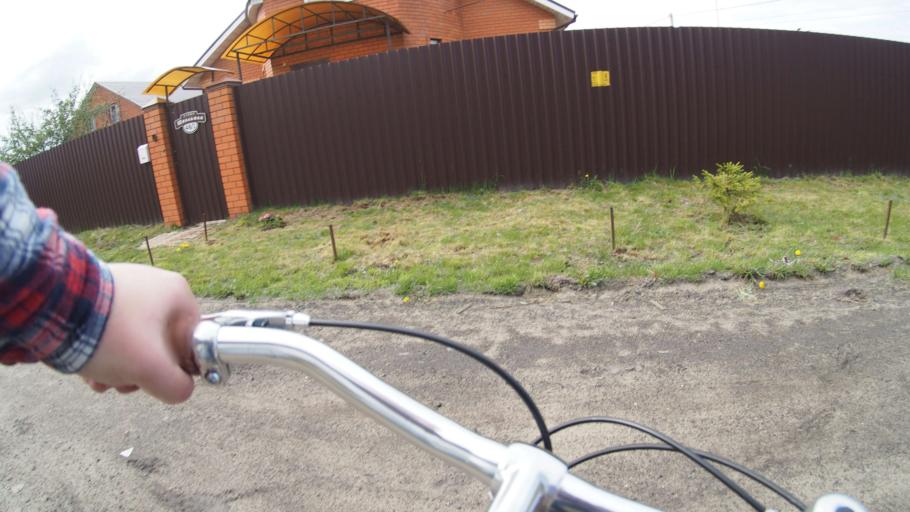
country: RU
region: Moskovskaya
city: Ramenskoye
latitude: 55.5508
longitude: 38.2460
